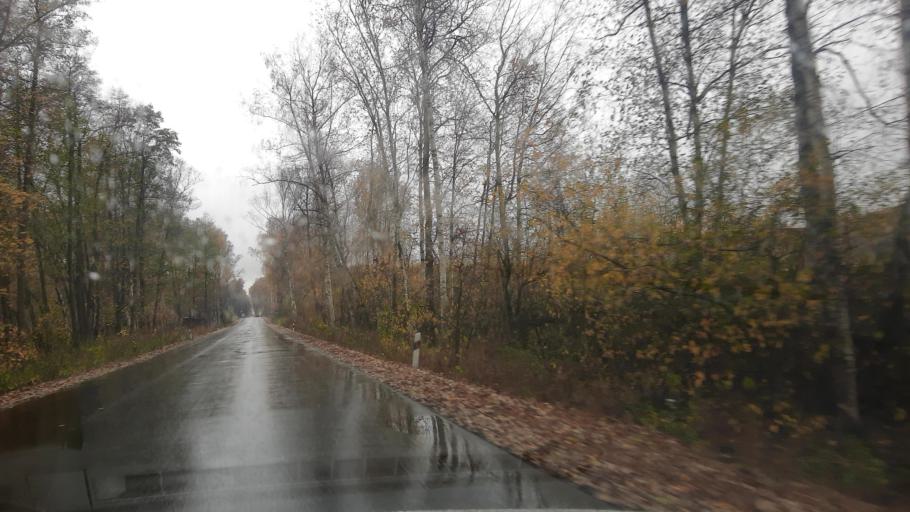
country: RU
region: Moskovskaya
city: Elektrostal'
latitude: 55.7970
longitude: 38.3718
